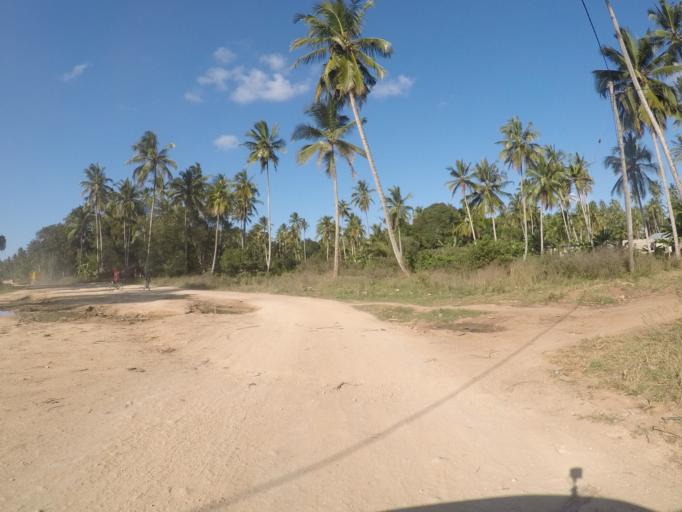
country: TZ
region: Zanzibar Central/South
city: Koani
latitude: -6.1754
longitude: 39.2838
